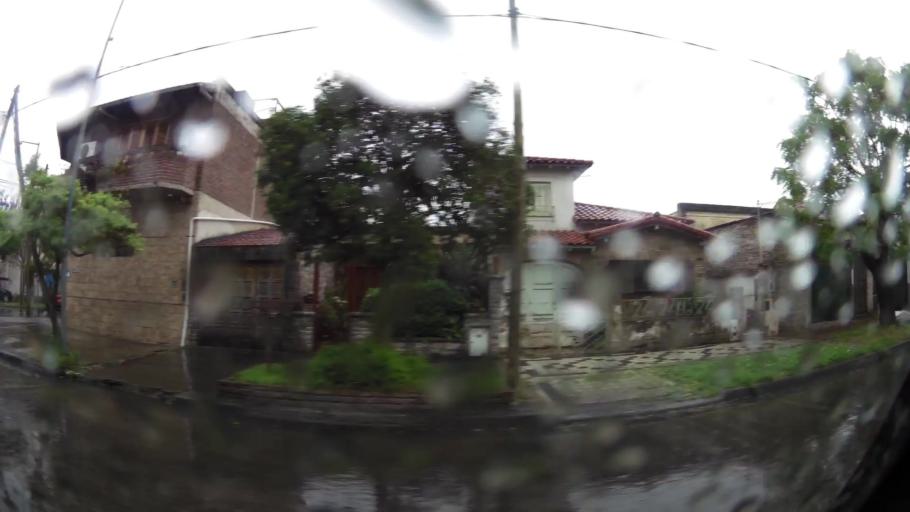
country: AR
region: Buenos Aires
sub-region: Partido de Lanus
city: Lanus
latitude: -34.6992
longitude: -58.4098
